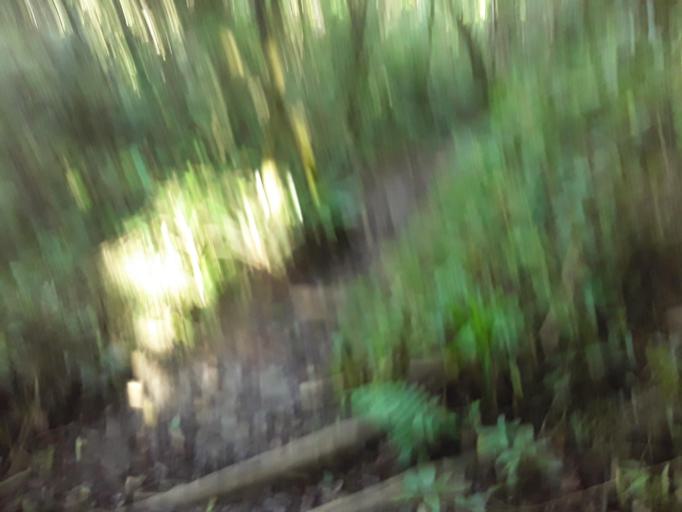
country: BR
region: Minas Gerais
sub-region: Lima Duarte
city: Lima Duarte
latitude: -21.6970
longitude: -43.8974
